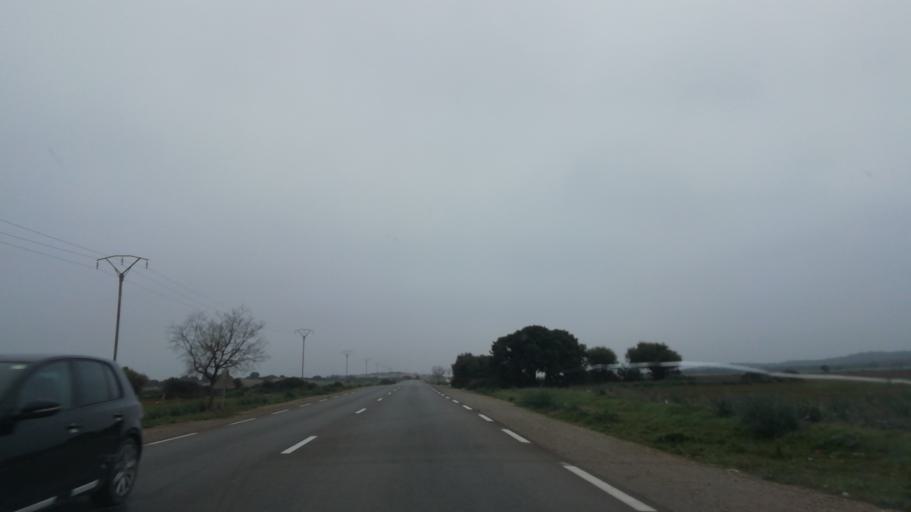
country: DZ
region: Mascara
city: Oued el Abtal
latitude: 35.3034
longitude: 0.4354
